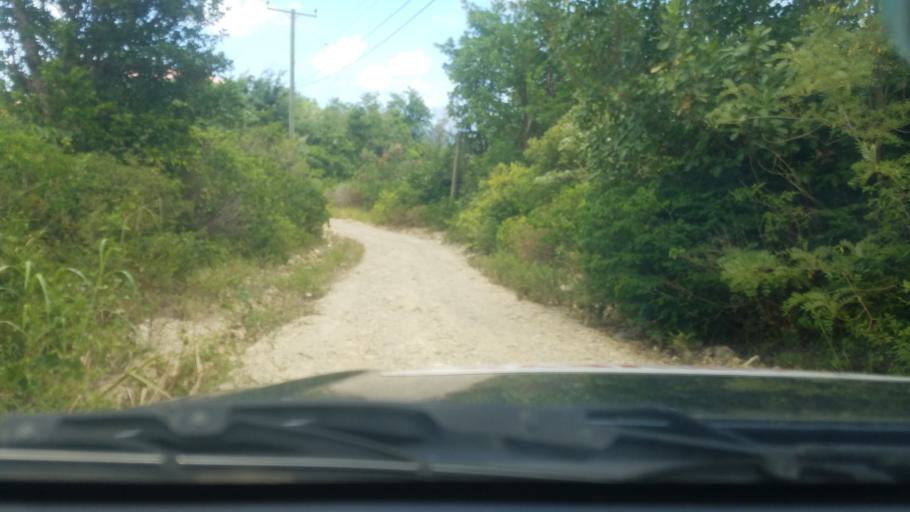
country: LC
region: Dennery Quarter
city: Dennery
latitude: 13.9198
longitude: -60.9009
